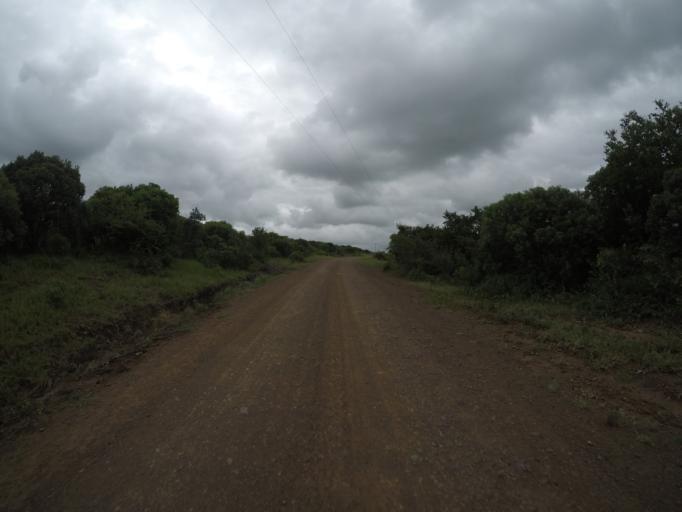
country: ZA
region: KwaZulu-Natal
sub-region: uThungulu District Municipality
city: Empangeni
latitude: -28.5699
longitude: 31.8736
